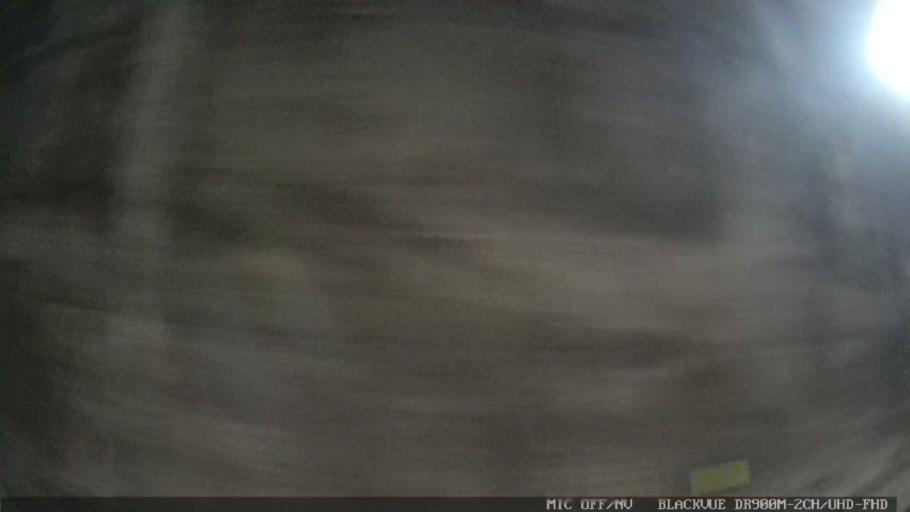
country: BR
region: Sao Paulo
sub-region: Cubatao
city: Cubatao
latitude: -23.8814
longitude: -46.4884
